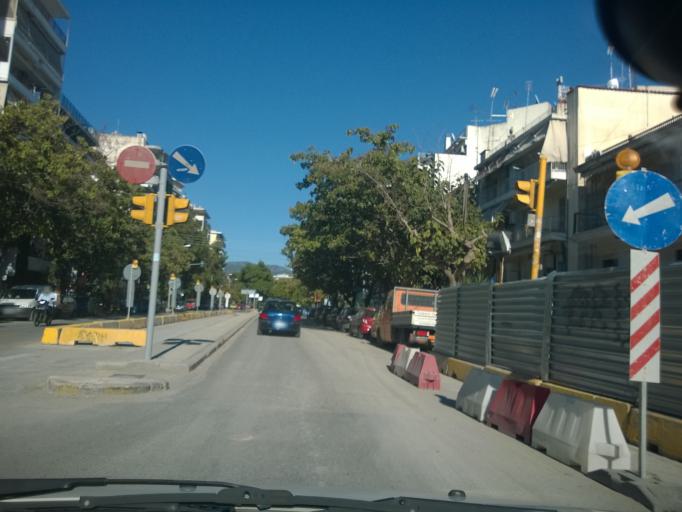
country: GR
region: Central Macedonia
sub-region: Nomos Thessalonikis
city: Kalamaria
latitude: 40.5957
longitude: 22.9609
